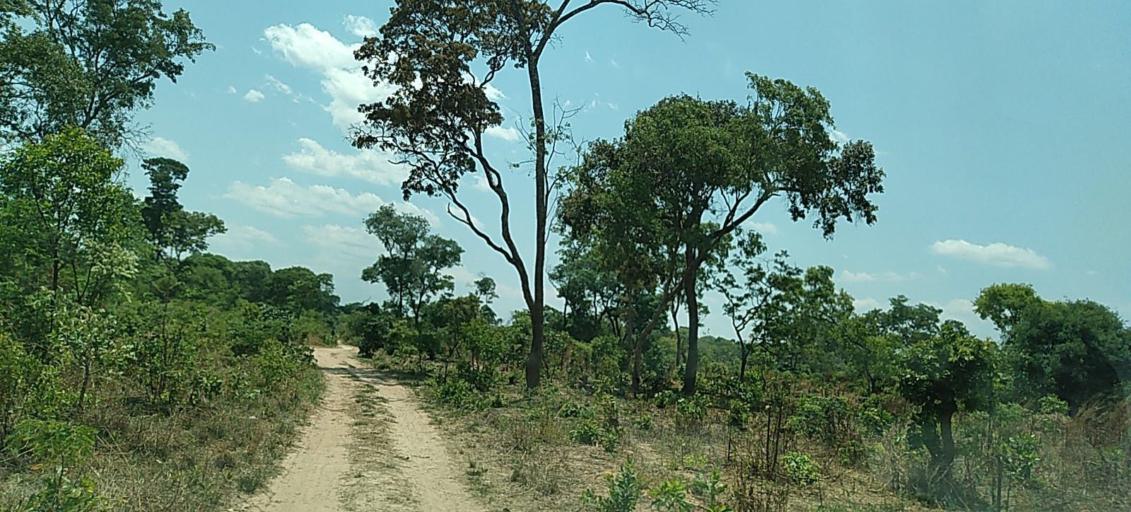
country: ZM
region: Central
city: Kapiri Mposhi
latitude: -13.6327
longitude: 28.7597
